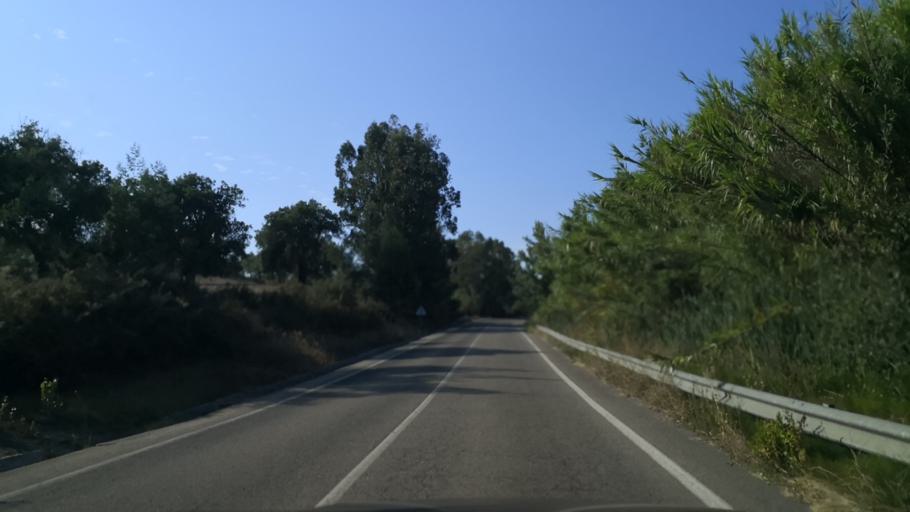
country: PT
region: Santarem
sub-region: Almeirim
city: Fazendas de Almeirim
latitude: 39.0868
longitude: -8.5716
